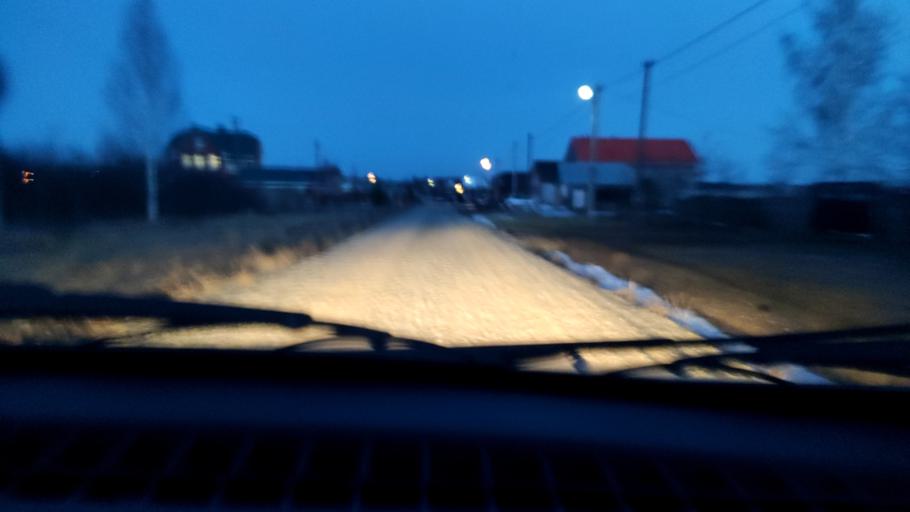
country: RU
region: Bashkortostan
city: Iglino
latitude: 54.7936
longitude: 56.3108
